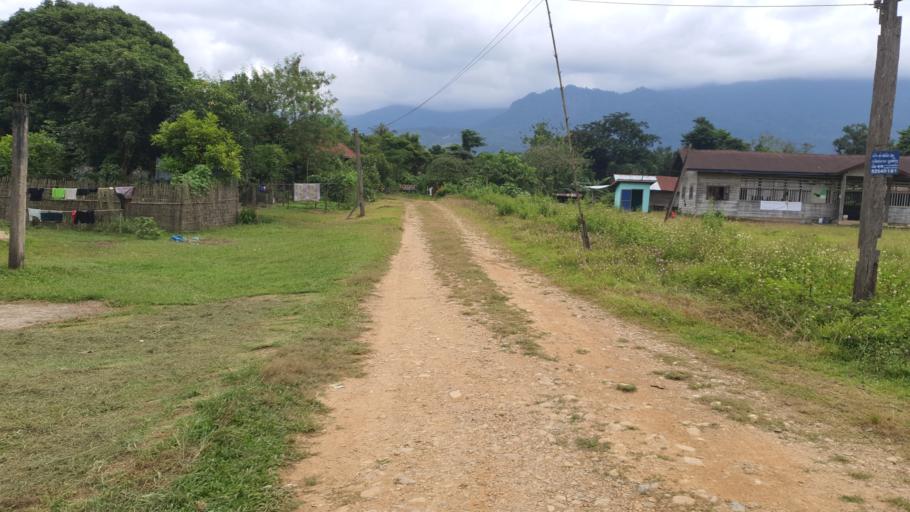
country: LA
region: Bolikhamxai
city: Bolikhan
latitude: 18.9503
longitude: 103.7881
